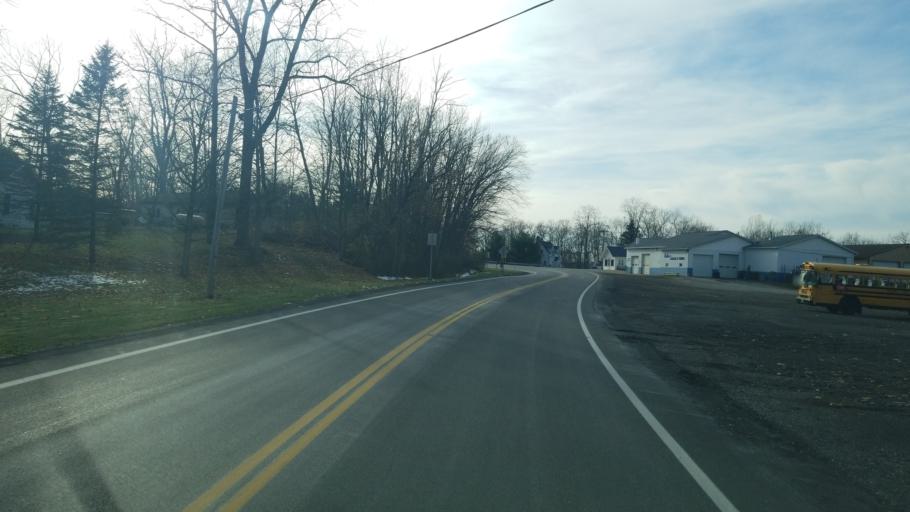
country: US
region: Ohio
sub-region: Ashland County
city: Ashland
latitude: 40.9260
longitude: -82.2799
